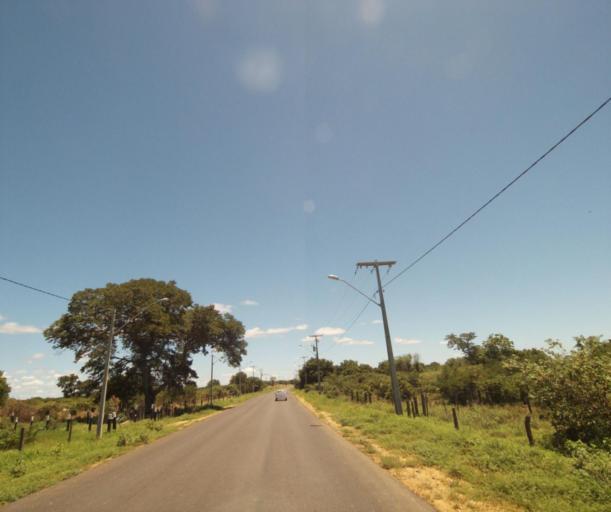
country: BR
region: Bahia
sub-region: Carinhanha
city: Carinhanha
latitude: -14.3164
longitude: -43.7783
